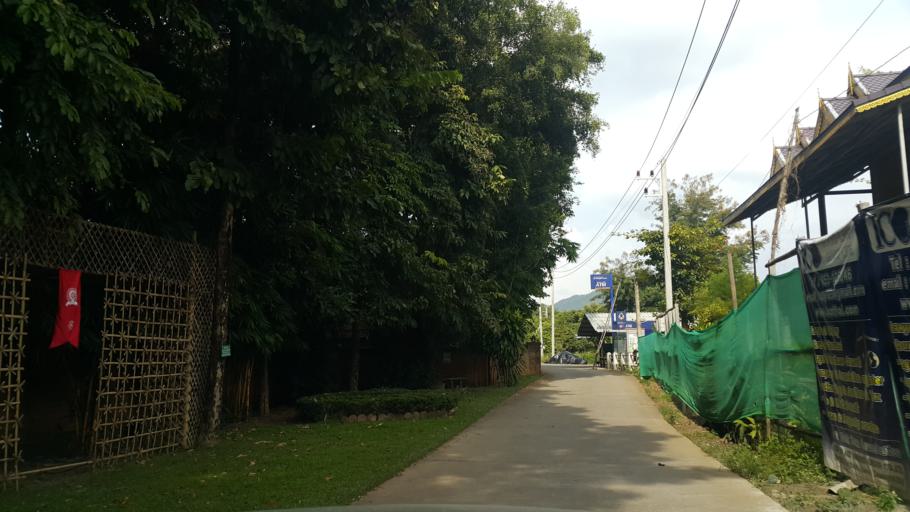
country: TH
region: Chiang Mai
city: San Sai
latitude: 18.9088
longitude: 99.1286
